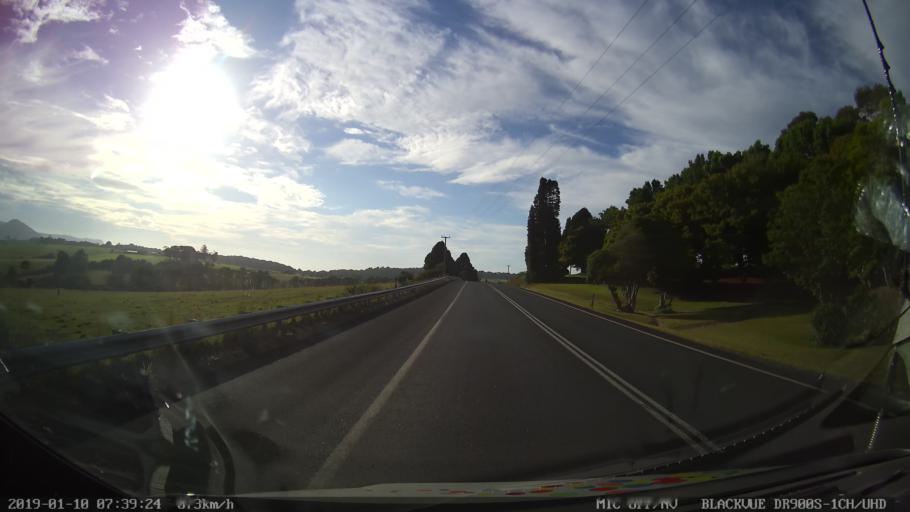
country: AU
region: New South Wales
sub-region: Bellingen
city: Dorrigo
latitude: -30.3570
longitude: 152.7187
